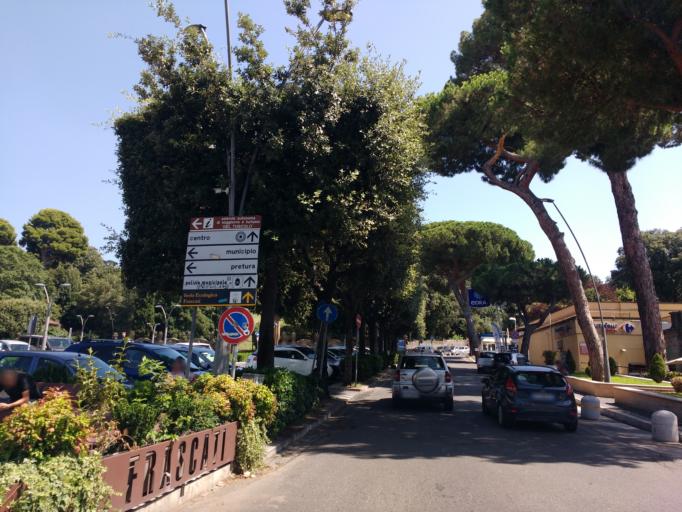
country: IT
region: Latium
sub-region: Citta metropolitana di Roma Capitale
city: Armetta
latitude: 41.8058
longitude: 12.6798
